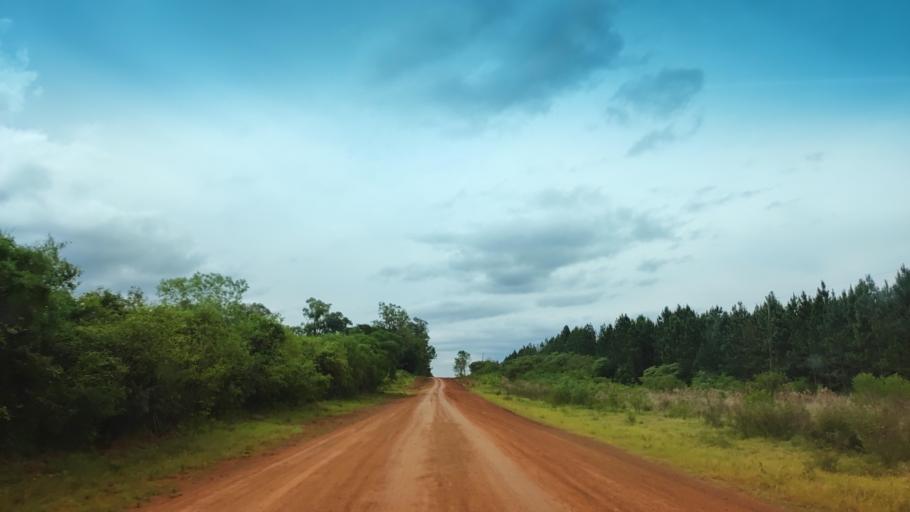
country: AR
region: Misiones
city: Garupa
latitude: -27.4970
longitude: -55.9708
